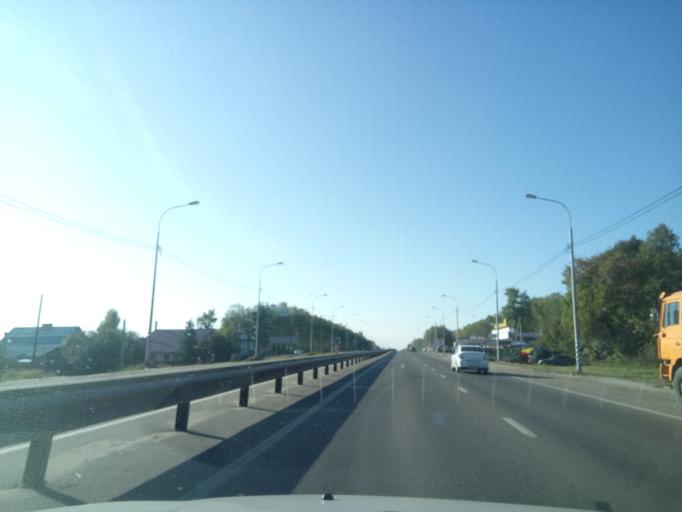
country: RU
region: Nizjnij Novgorod
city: Nizhniy Novgorod
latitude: 56.2138
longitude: 43.9296
